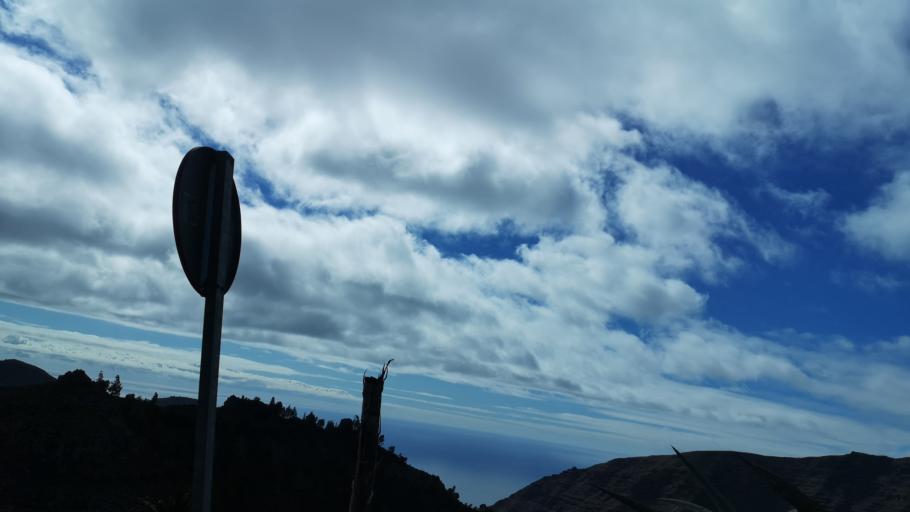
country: ES
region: Canary Islands
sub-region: Provincia de Santa Cruz de Tenerife
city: Vallehermosa
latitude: 28.1217
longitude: -17.3169
